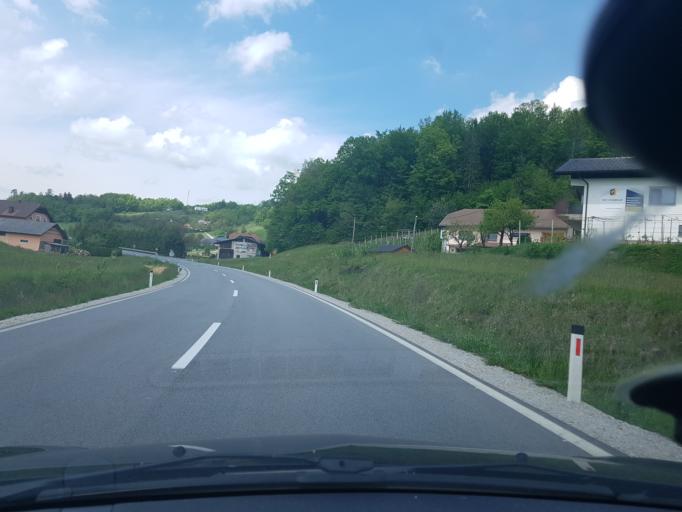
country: SI
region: Rogaska Slatina
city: Rogaska Slatina
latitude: 46.2403
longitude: 15.6699
